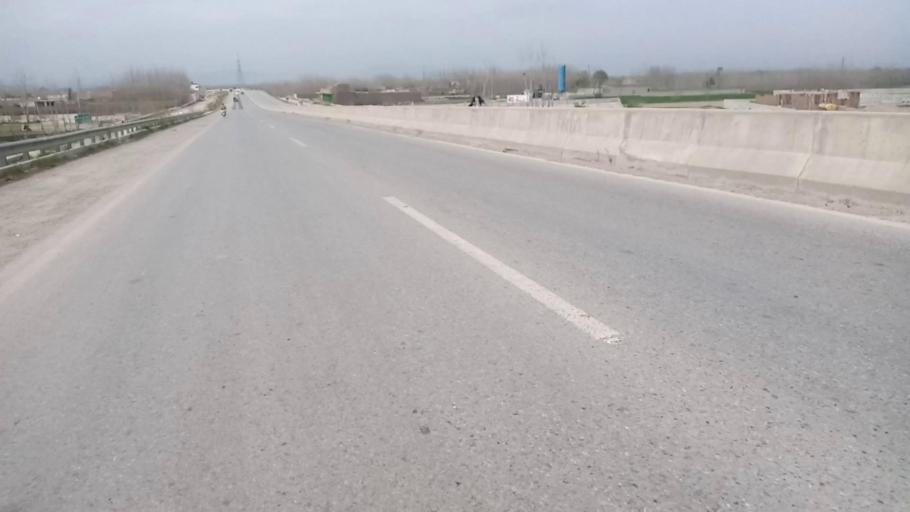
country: PK
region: Khyber Pakhtunkhwa
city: Peshawar
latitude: 34.0498
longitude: 71.6141
